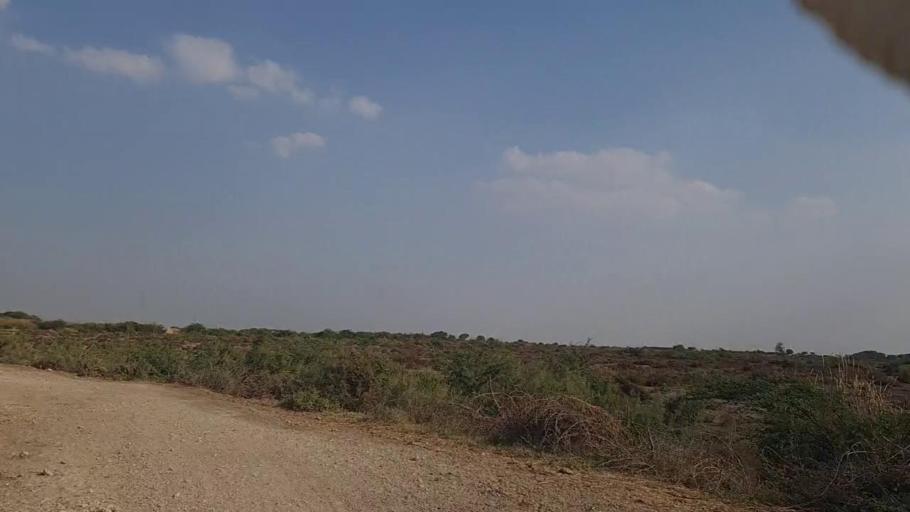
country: PK
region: Sindh
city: Jati
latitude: 24.4298
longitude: 68.3696
